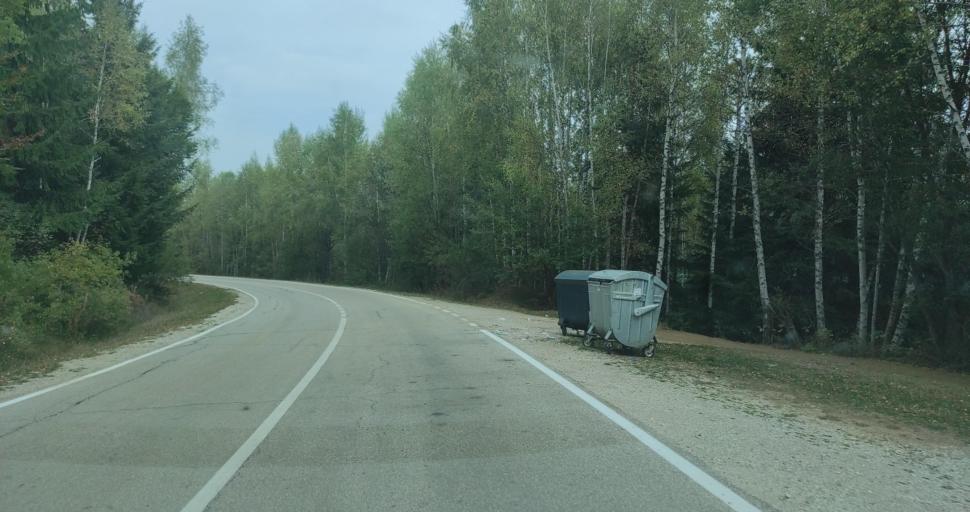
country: RS
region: Central Serbia
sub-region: Jablanicki Okrug
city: Crna Trava
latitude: 42.7309
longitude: 22.3352
